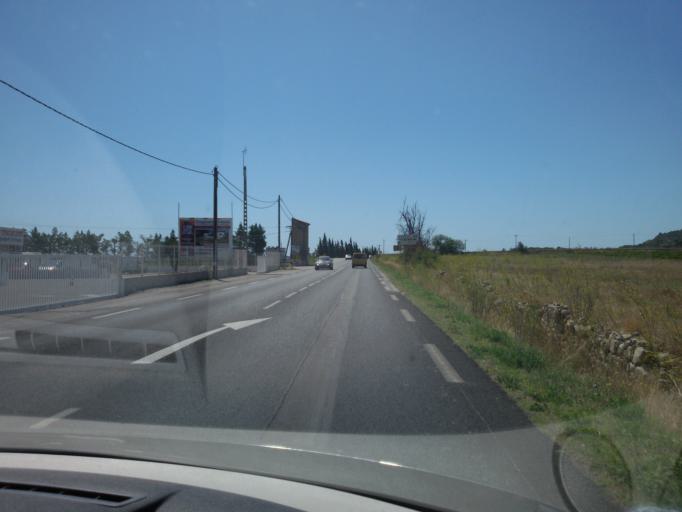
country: FR
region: Languedoc-Roussillon
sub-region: Departement de l'Herault
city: Vic-la-Gardiole
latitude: 43.4757
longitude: 3.7708
